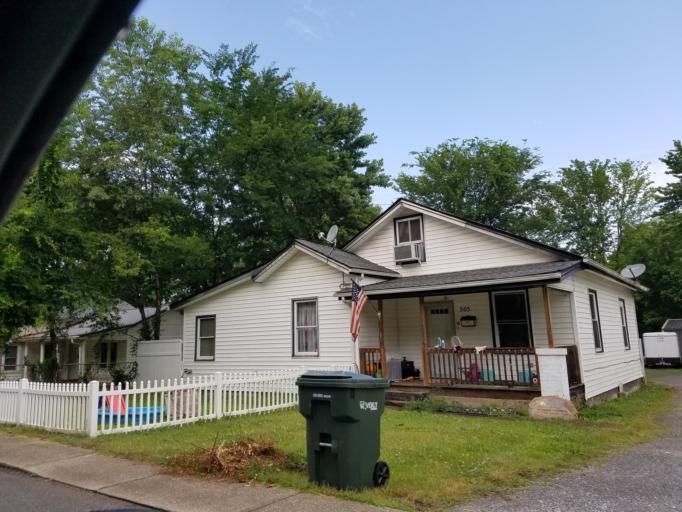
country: US
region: Tennessee
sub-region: Humphreys County
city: Waverly
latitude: 36.0821
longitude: -87.7805
